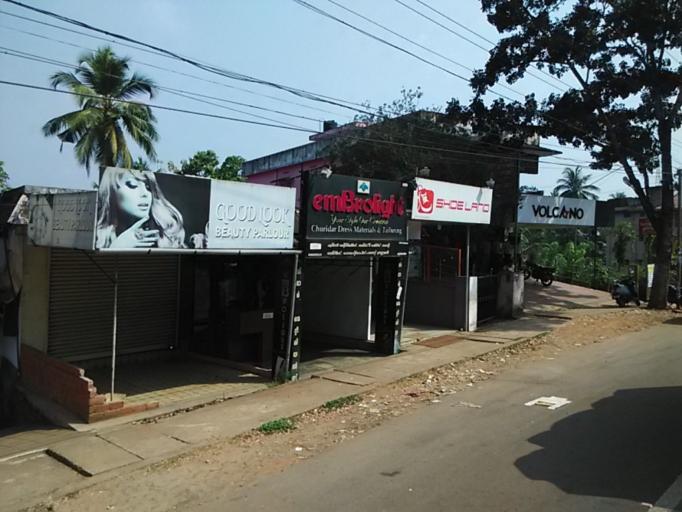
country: IN
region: Kerala
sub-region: Kozhikode
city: Kunnamangalam
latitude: 11.3040
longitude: 75.8754
